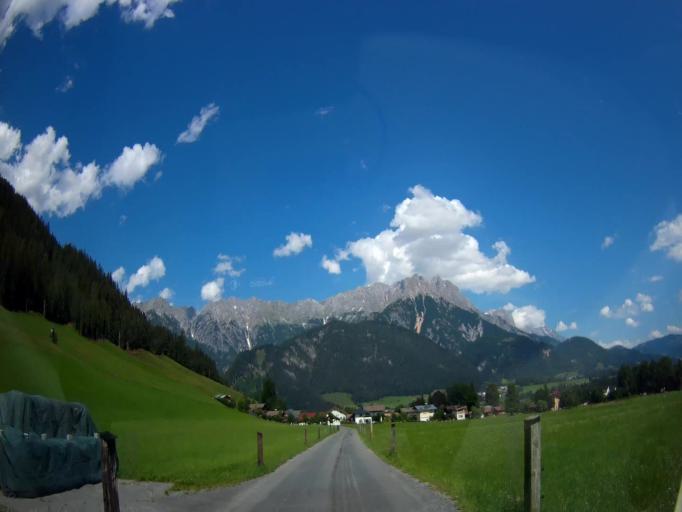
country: AT
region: Salzburg
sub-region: Politischer Bezirk Zell am See
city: Leogang
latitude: 47.4502
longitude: 12.8034
